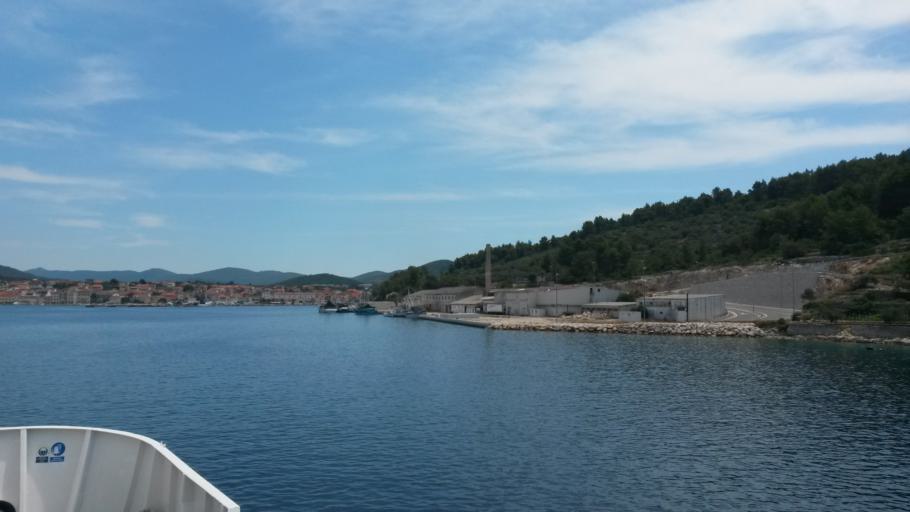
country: HR
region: Dubrovacko-Neretvanska
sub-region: Grad Dubrovnik
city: Vela Luka
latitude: 42.9614
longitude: 16.7017
